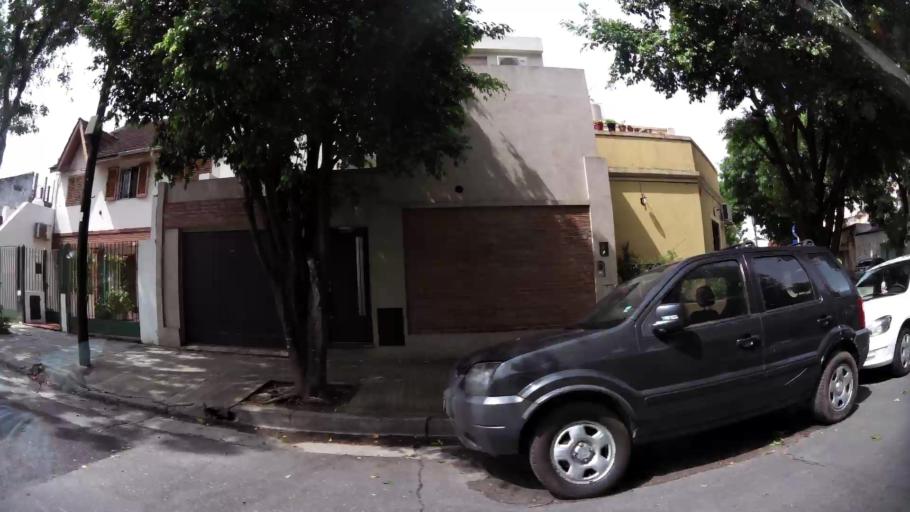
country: AR
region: Buenos Aires
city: Caseros
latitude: -34.6186
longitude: -58.5291
